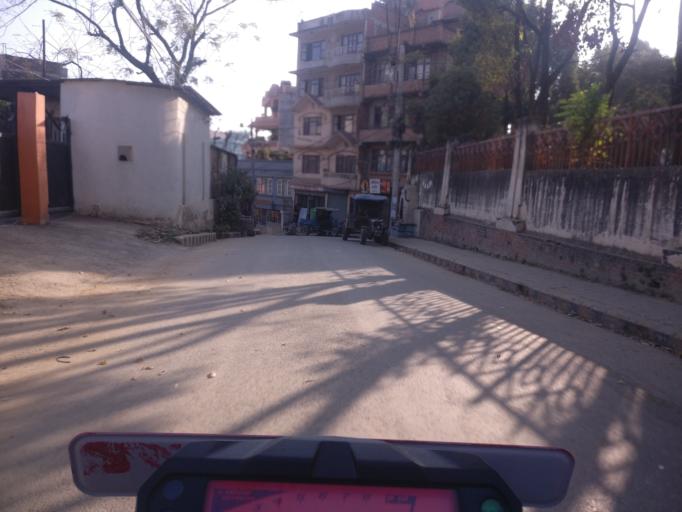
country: NP
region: Central Region
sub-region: Bagmati Zone
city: Patan
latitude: 27.6612
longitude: 85.3293
